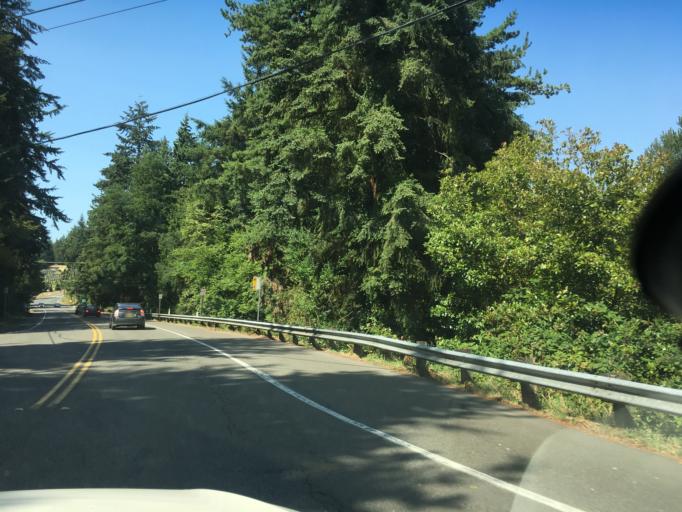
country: US
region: Washington
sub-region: King County
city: Shoreline
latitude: 47.7472
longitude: -122.3533
